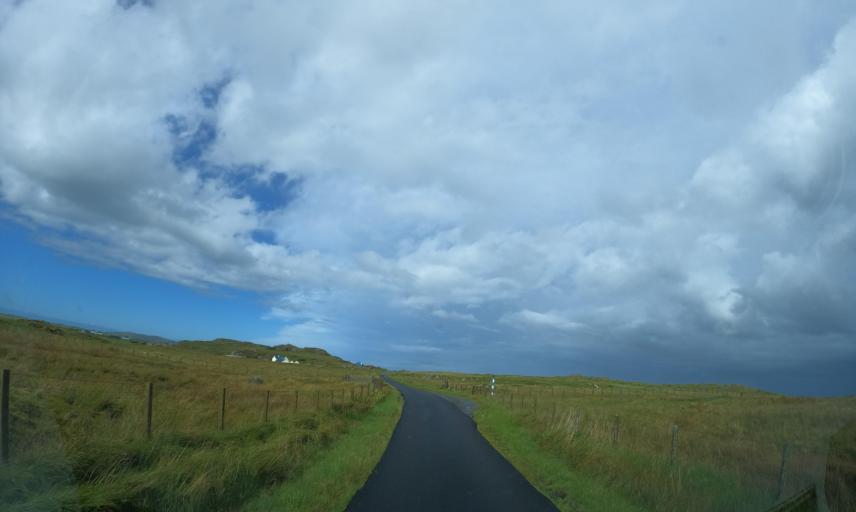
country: GB
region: Scotland
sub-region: Eilean Siar
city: Barra
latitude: 56.5229
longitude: -6.8457
